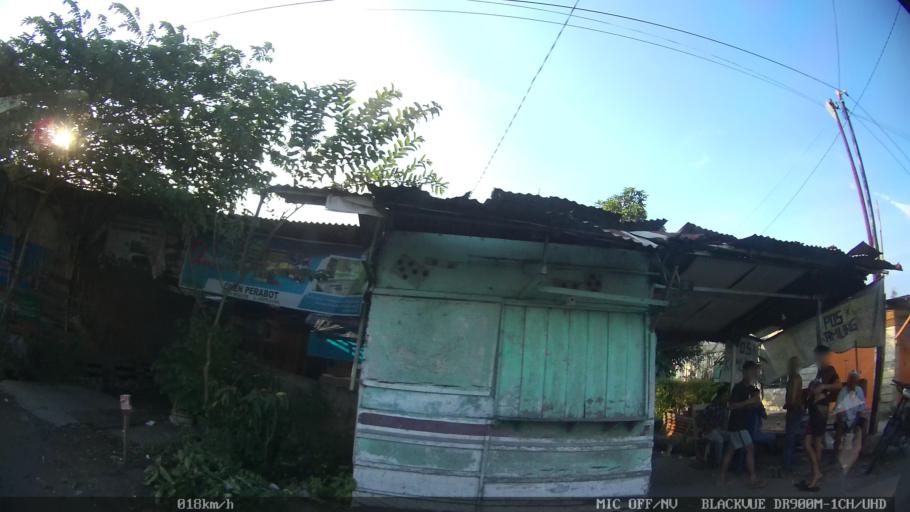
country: ID
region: North Sumatra
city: Medan
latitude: 3.6242
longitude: 98.6621
